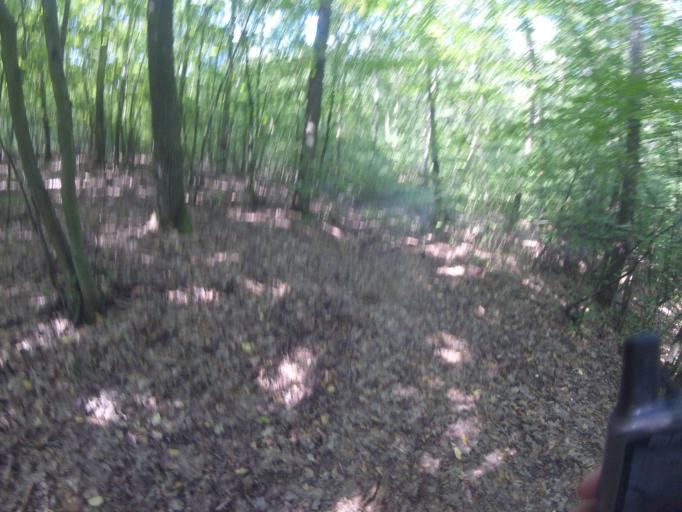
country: HU
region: Nograd
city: Bujak
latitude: 47.9038
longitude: 19.5141
